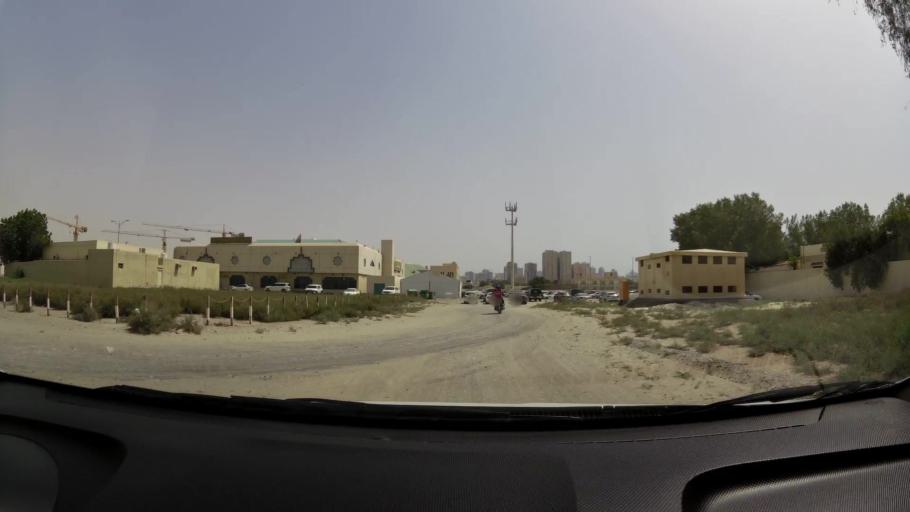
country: AE
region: Ash Shariqah
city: Sharjah
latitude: 25.3513
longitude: 55.4091
